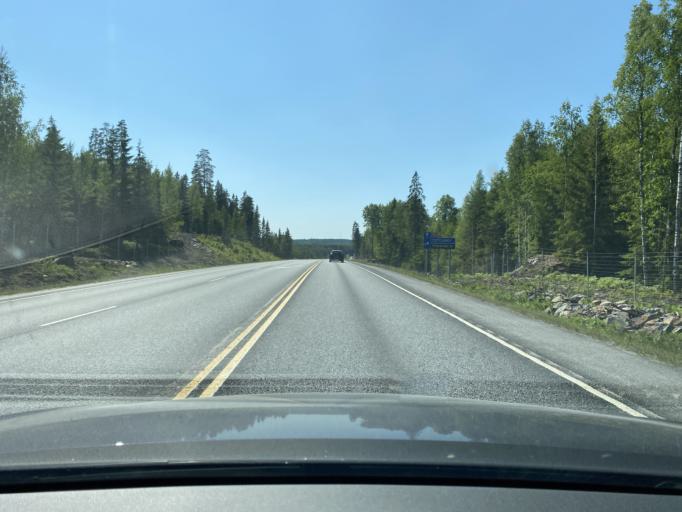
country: FI
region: Pirkanmaa
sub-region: Tampere
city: Nokia
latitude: 61.4076
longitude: 23.2923
